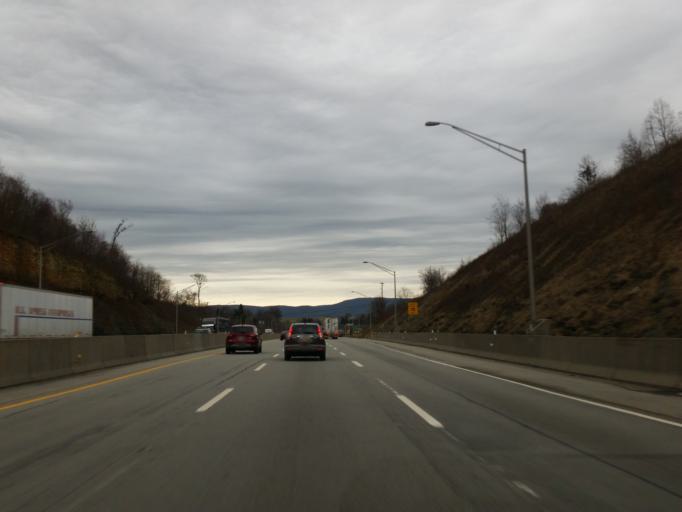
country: US
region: Pennsylvania
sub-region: Fayette County
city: Bear Rocks
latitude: 40.1121
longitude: -79.3880
